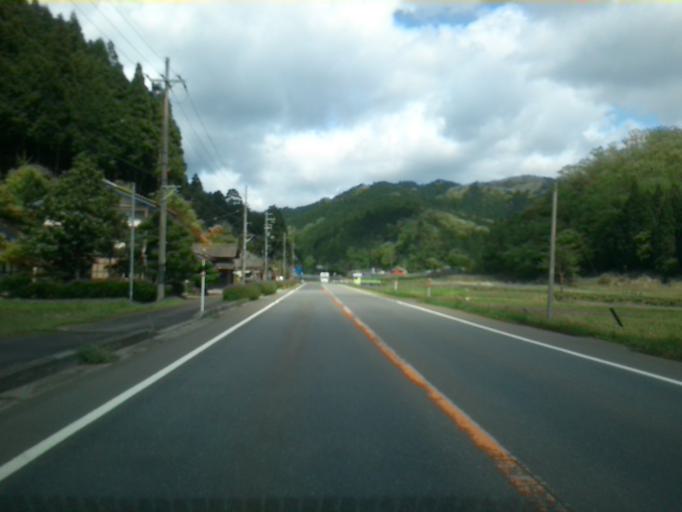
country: JP
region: Kyoto
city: Fukuchiyama
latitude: 35.4204
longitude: 135.0217
